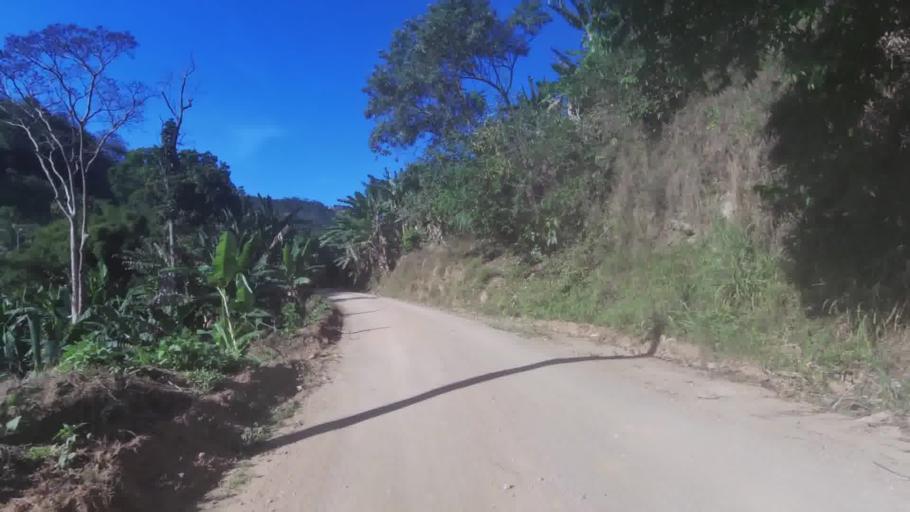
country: BR
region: Espirito Santo
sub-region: Iconha
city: Iconha
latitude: -20.7595
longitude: -40.8203
